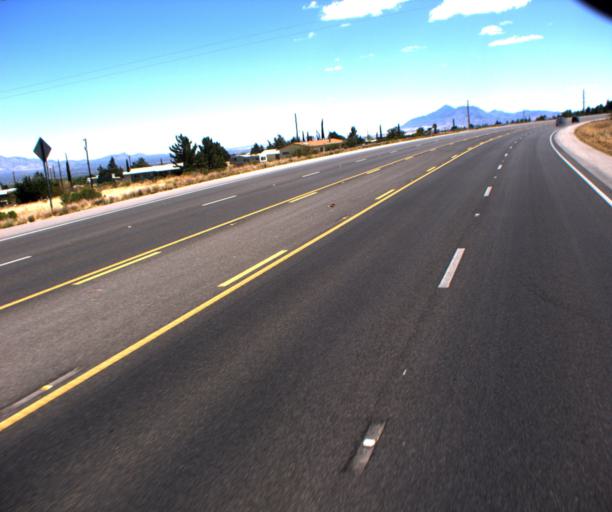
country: US
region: Arizona
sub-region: Cochise County
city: Sierra Vista Southeast
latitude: 31.4341
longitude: -110.2437
